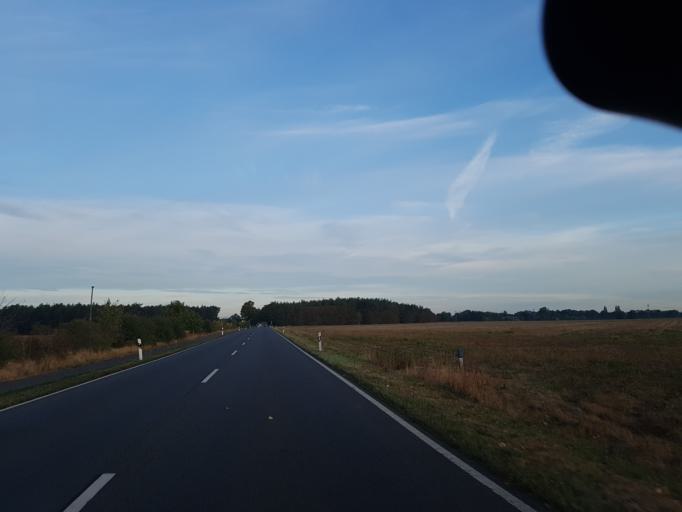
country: DE
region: Brandenburg
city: Sonnewalde
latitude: 51.6601
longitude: 13.6548
